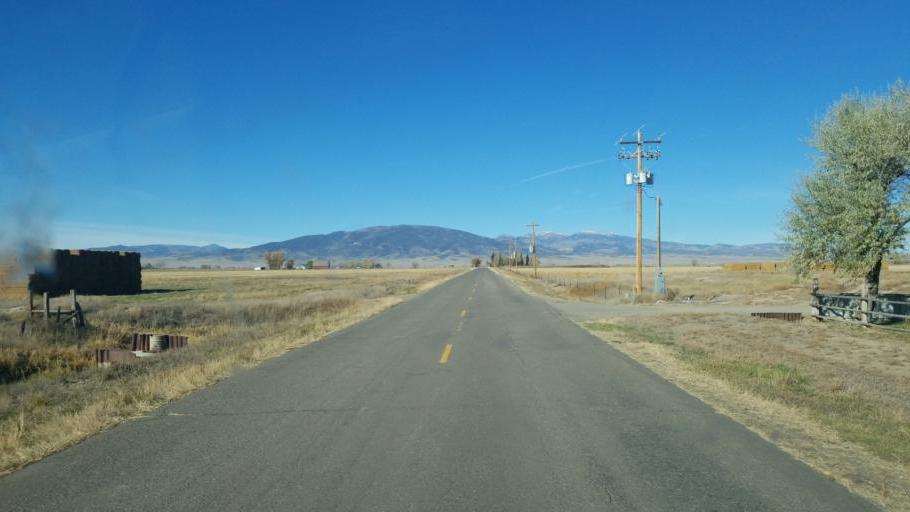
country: US
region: Colorado
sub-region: Rio Grande County
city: Monte Vista
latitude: 37.4591
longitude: -106.0663
